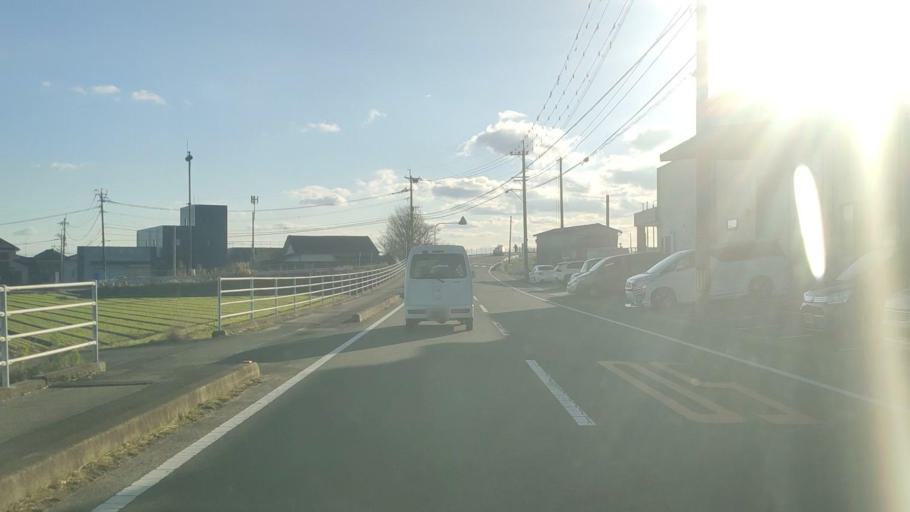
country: JP
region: Saga Prefecture
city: Saga-shi
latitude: 33.2854
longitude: 130.2325
